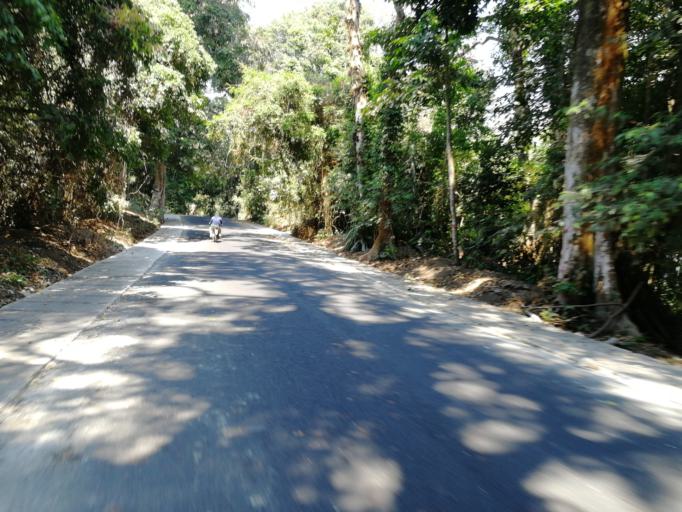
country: ID
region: West Nusa Tenggara
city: Lelongken
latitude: -8.3210
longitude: 116.4934
